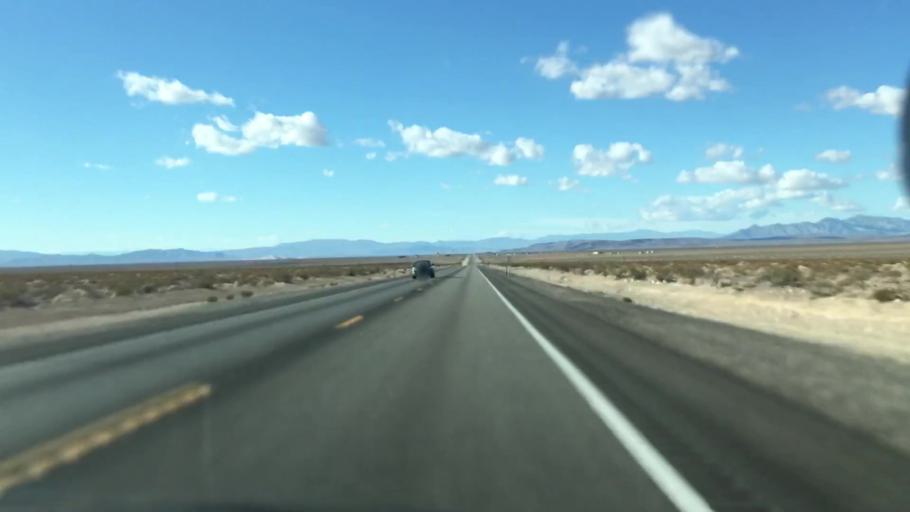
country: US
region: Nevada
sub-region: Nye County
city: Beatty
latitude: 36.6335
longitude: -116.3582
